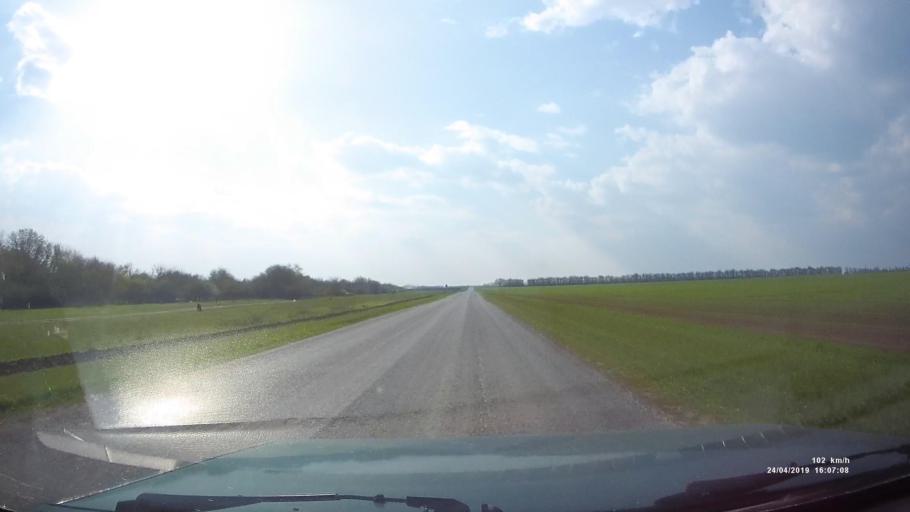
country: RU
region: Rostov
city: Sovetskoye
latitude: 46.6898
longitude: 42.3357
